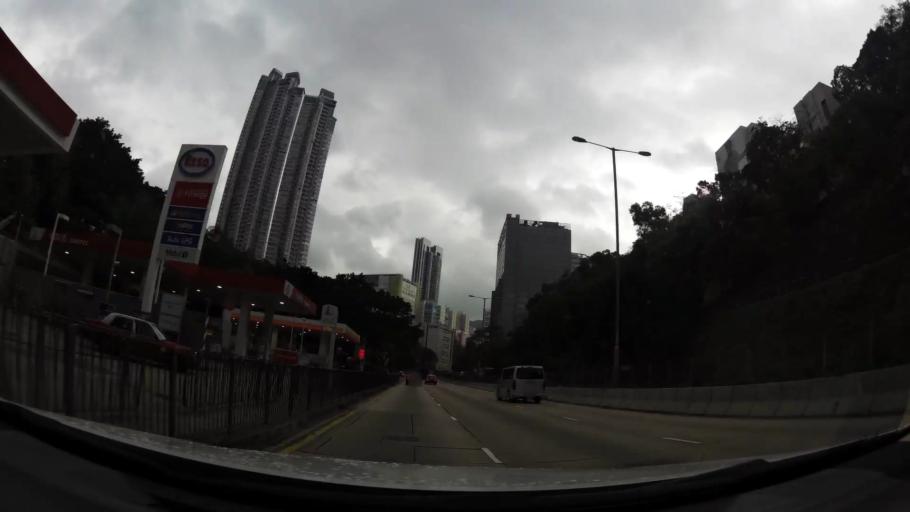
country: HK
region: Tsuen Wan
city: Tsuen Wan
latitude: 22.3709
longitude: 114.1276
